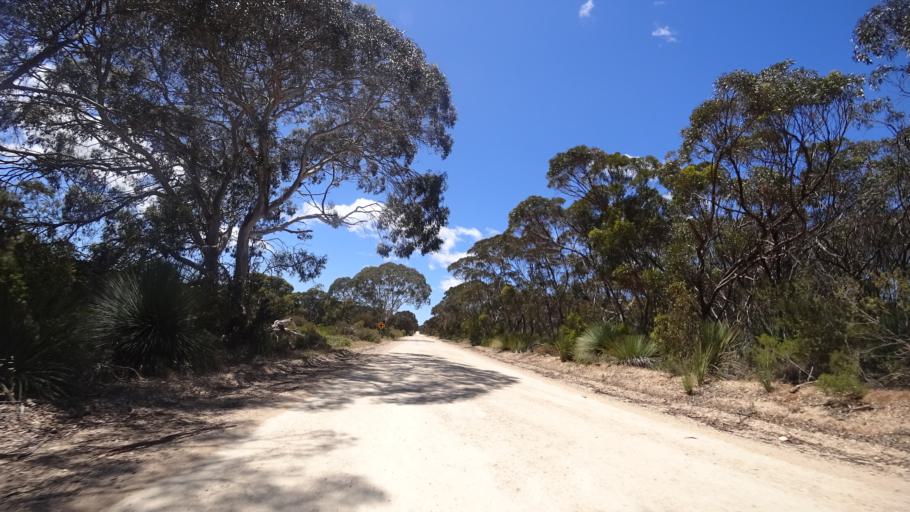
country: AU
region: South Australia
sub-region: Kangaroo Island
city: Kingscote
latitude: -35.8262
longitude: 138.0126
